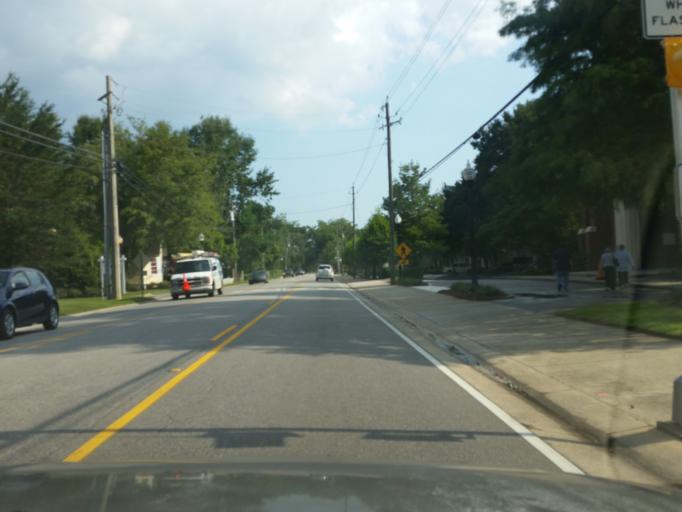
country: US
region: Alabama
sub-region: Baldwin County
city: Daphne
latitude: 30.6011
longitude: -87.9028
